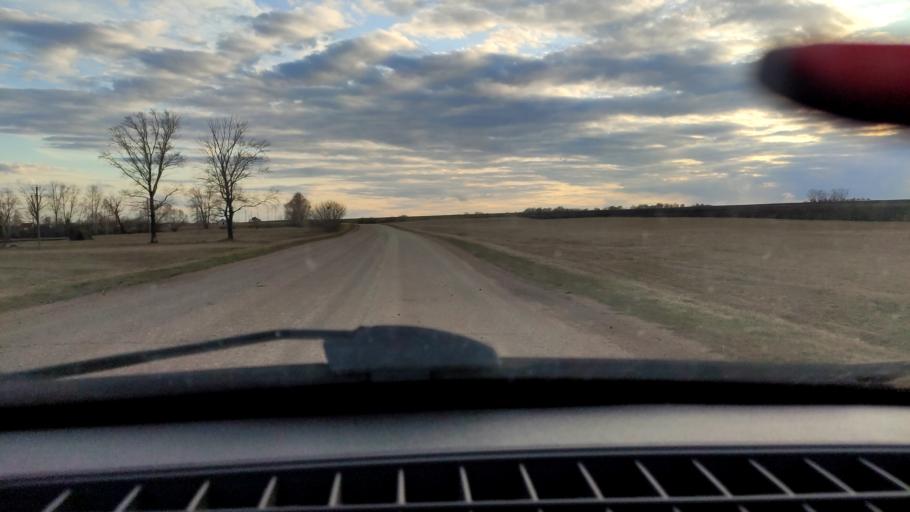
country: RU
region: Bashkortostan
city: Tolbazy
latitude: 54.0060
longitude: 55.6859
